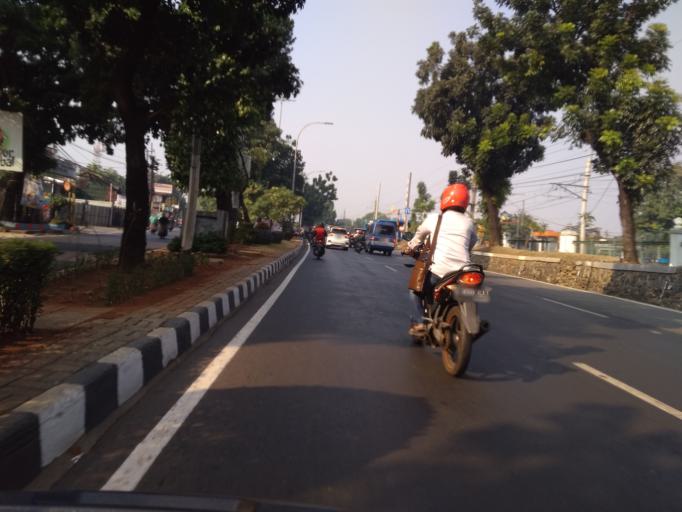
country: ID
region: Jakarta Raya
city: Jakarta
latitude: -6.2977
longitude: 106.8405
